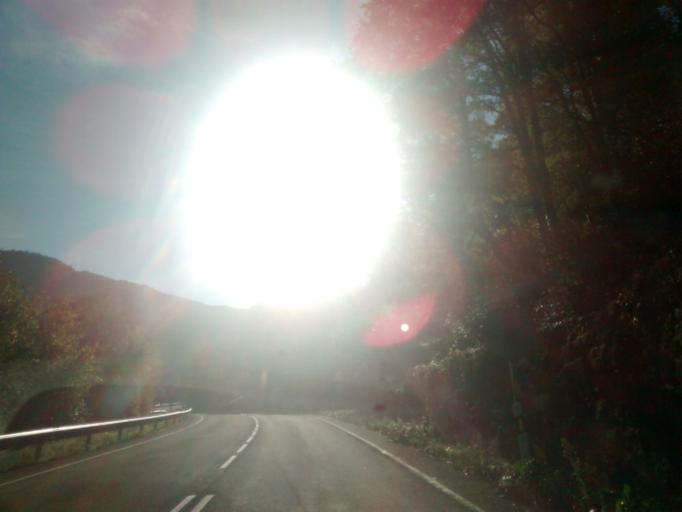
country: ES
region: Cantabria
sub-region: Provincia de Cantabria
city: Santiurde de Toranzo
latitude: 43.1627
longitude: -3.8986
